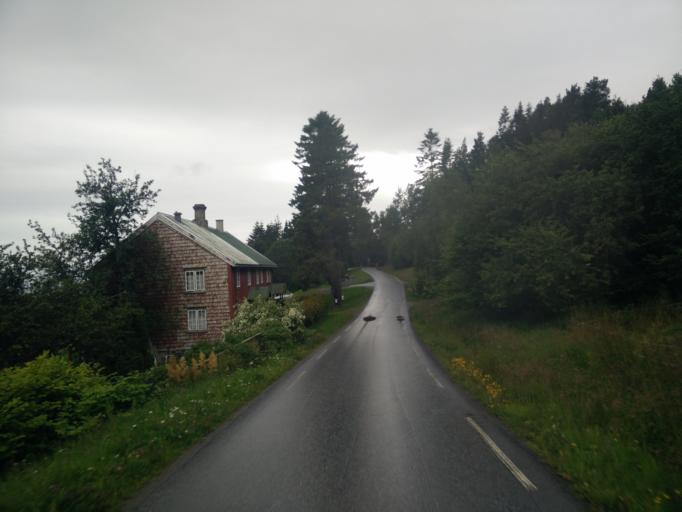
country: NO
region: More og Romsdal
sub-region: Kristiansund
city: Rensvik
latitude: 63.0167
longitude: 7.9054
